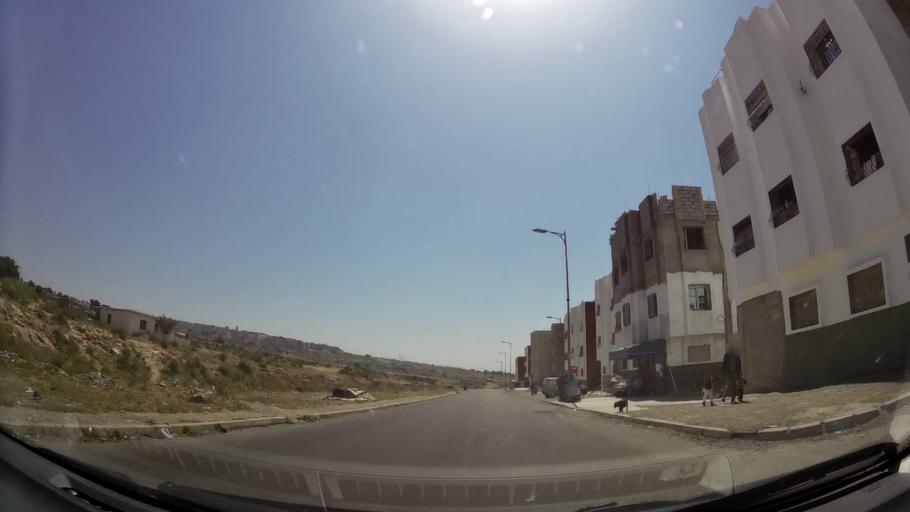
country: MA
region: Oued ed Dahab-Lagouira
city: Dakhla
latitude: 30.4422
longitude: -9.5556
